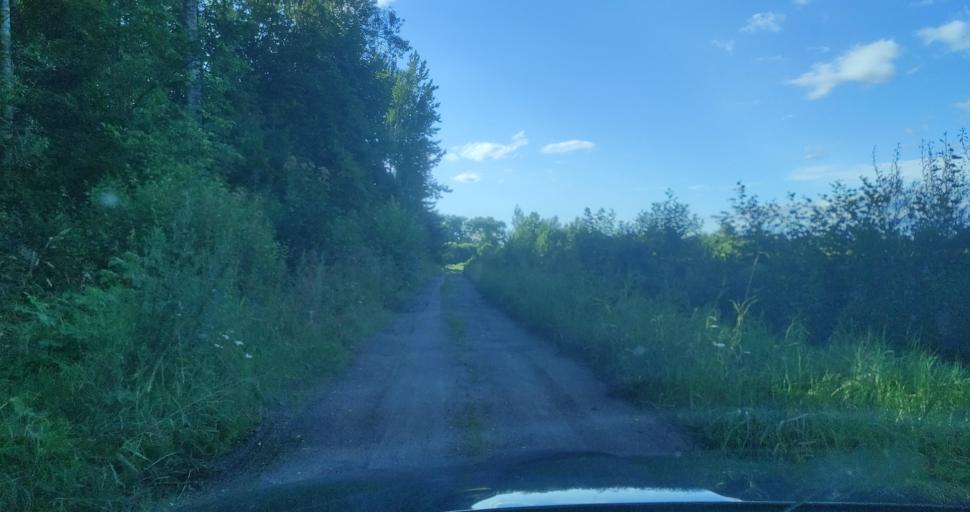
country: LV
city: Tireli
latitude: 56.7035
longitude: 23.4601
